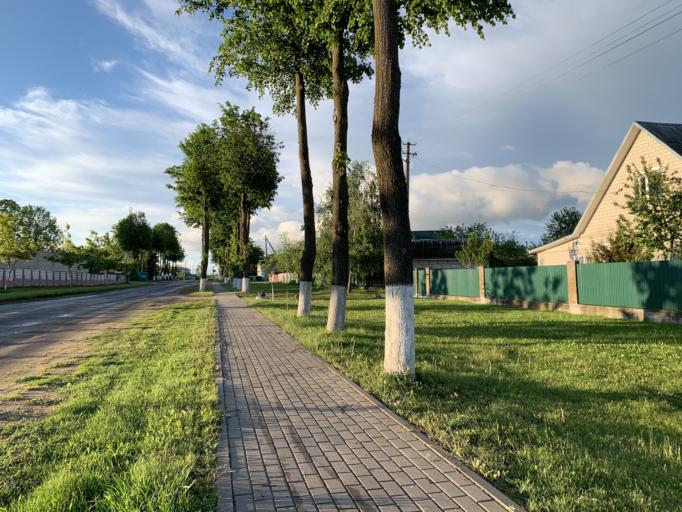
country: BY
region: Minsk
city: Nyasvizh
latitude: 53.2108
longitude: 26.6971
